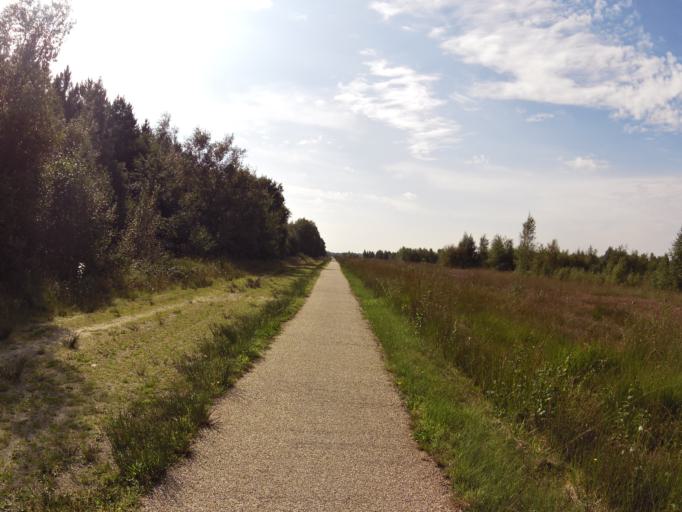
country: DE
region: Lower Saxony
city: Twist
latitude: 52.6708
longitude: 7.0578
